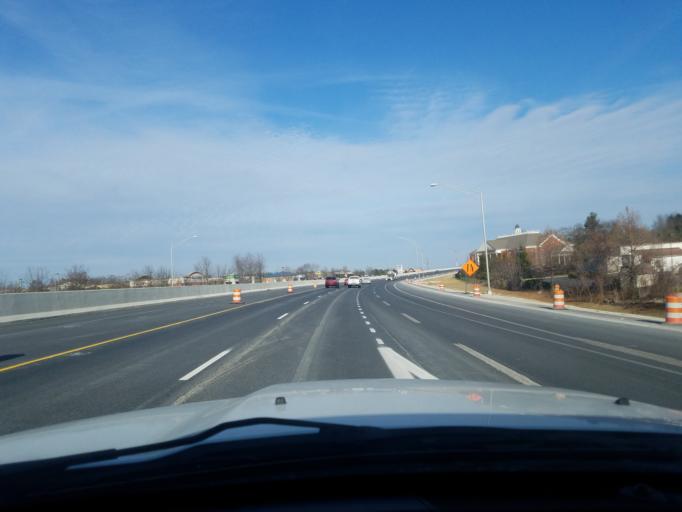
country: US
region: Indiana
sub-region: Monroe County
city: Bloomington
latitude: 39.1680
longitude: -86.5724
